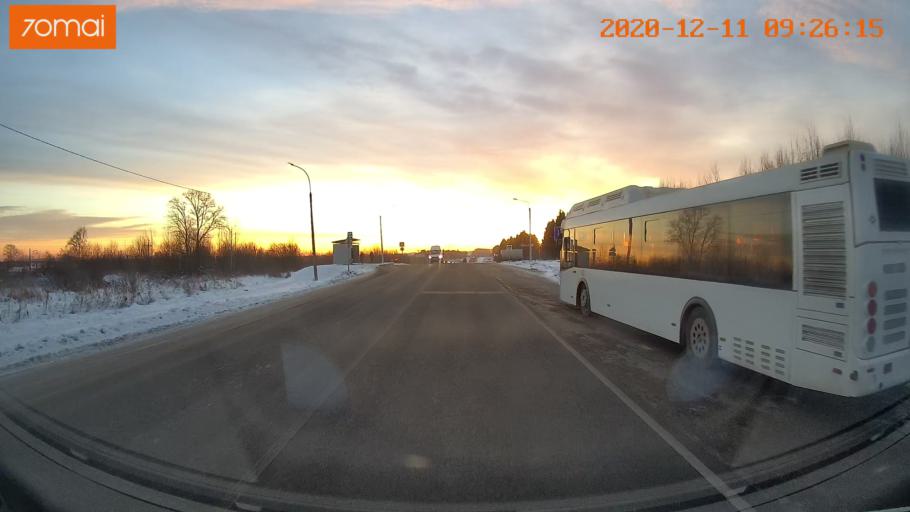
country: RU
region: Vologda
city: Vologda
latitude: 59.1709
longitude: 39.9862
